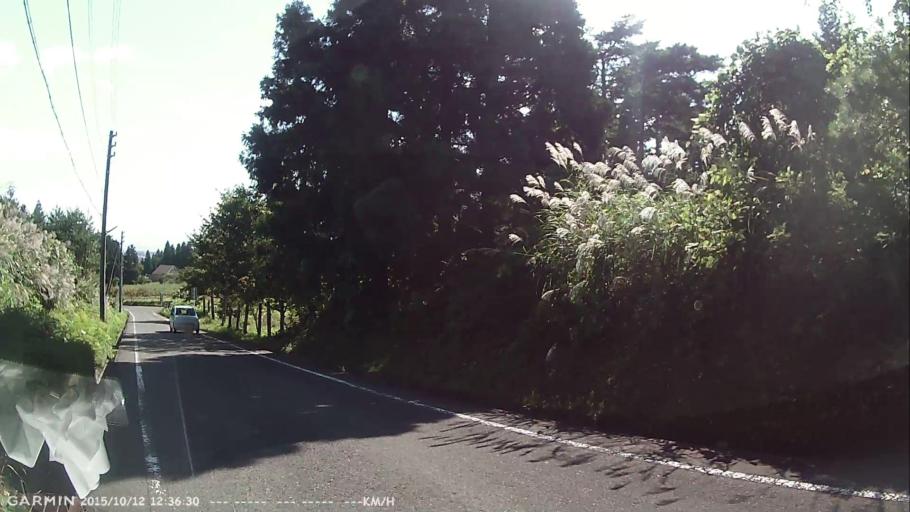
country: JP
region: Fukushima
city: Kitakata
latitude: 37.5880
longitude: 139.8006
